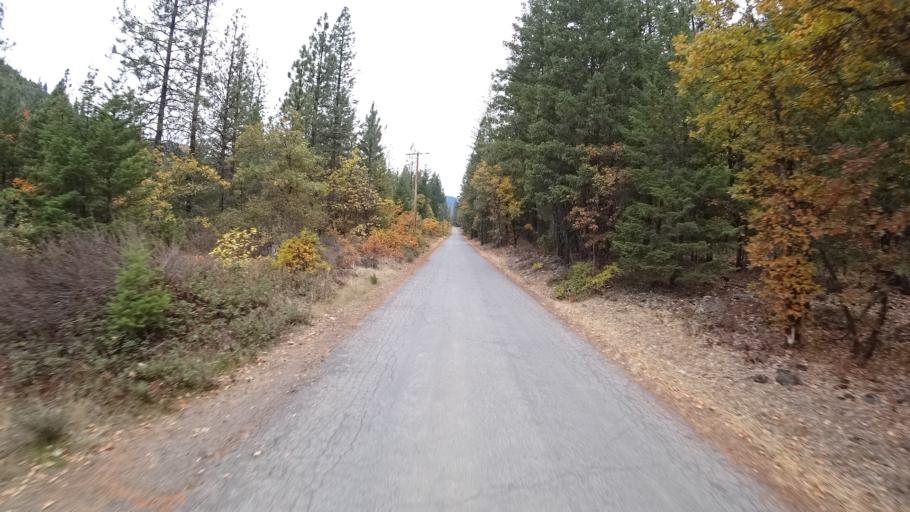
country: US
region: California
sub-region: Siskiyou County
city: Happy Camp
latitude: 41.8807
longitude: -123.4327
